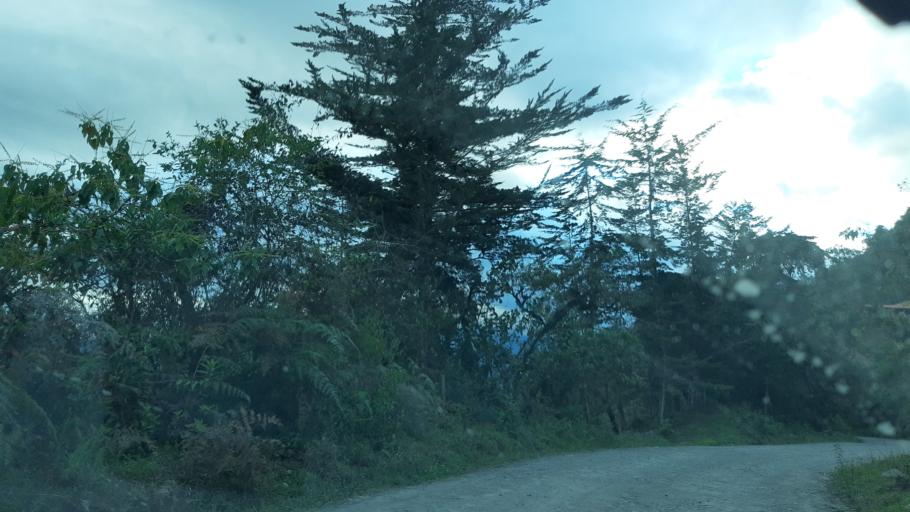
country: CO
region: Boyaca
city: Garagoa
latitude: 5.0844
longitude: -73.3197
